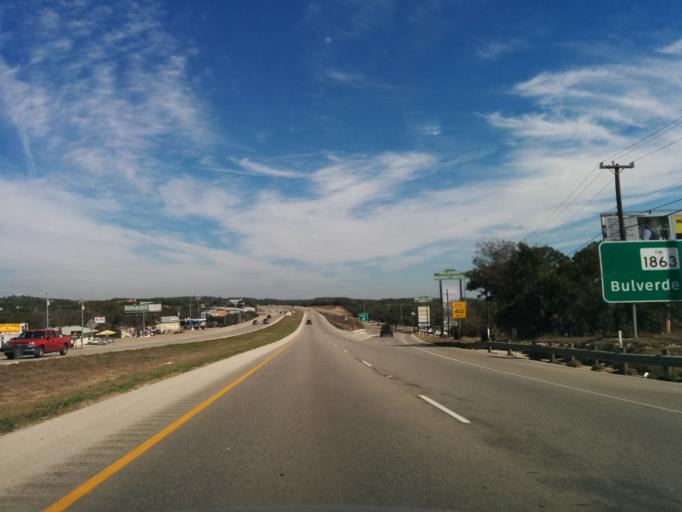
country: US
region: Texas
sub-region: Comal County
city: Bulverde
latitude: 29.7399
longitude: -98.4374
